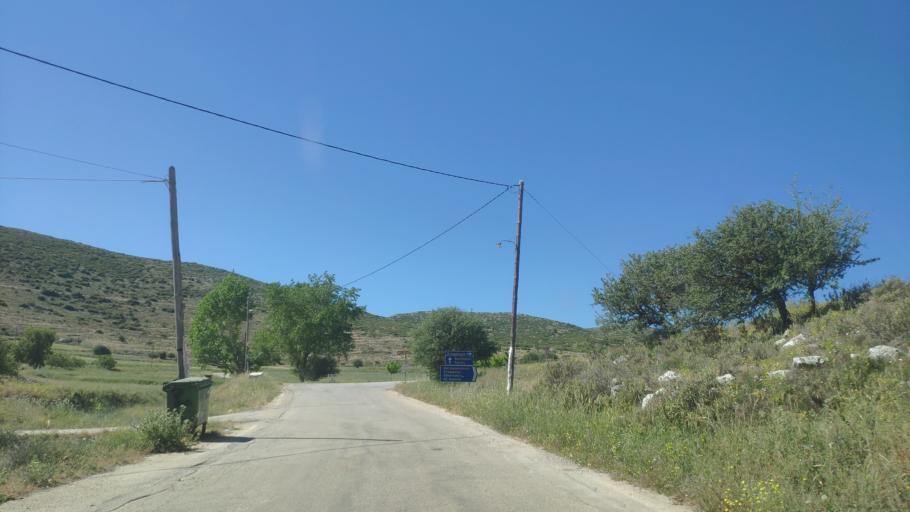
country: GR
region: Peloponnese
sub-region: Nomos Korinthias
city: Khiliomodhi
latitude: 37.7538
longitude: 22.8738
